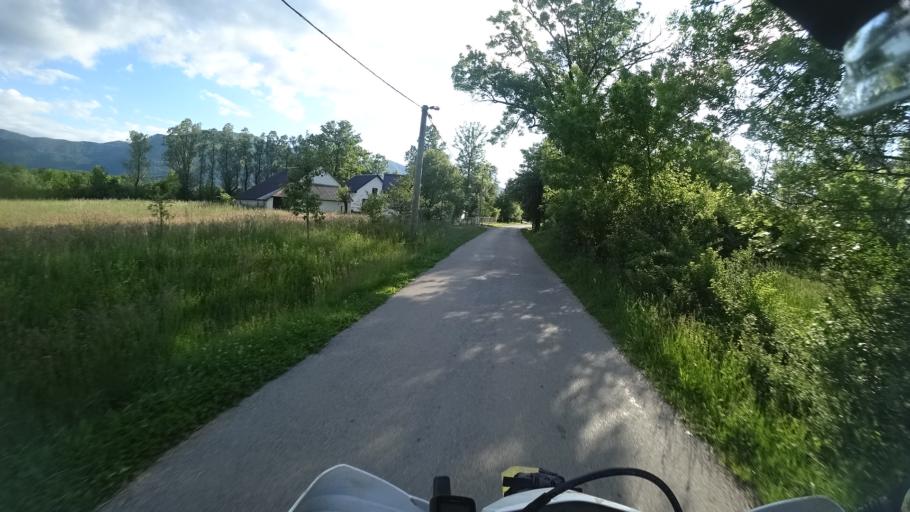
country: HR
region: Licko-Senjska
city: Gospic
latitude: 44.5126
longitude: 15.3216
